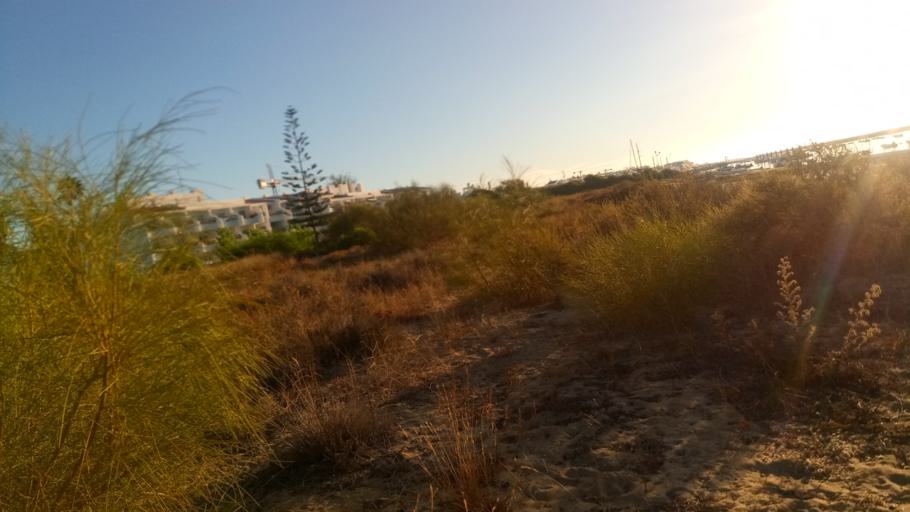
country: PT
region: Faro
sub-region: Tavira
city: Tavira
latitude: 37.1328
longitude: -7.6046
